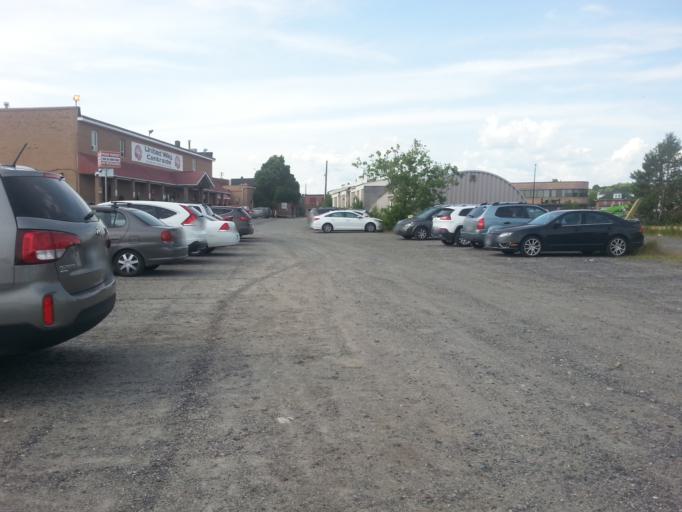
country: CA
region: Ontario
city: Greater Sudbury
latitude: 46.4919
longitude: -80.9978
